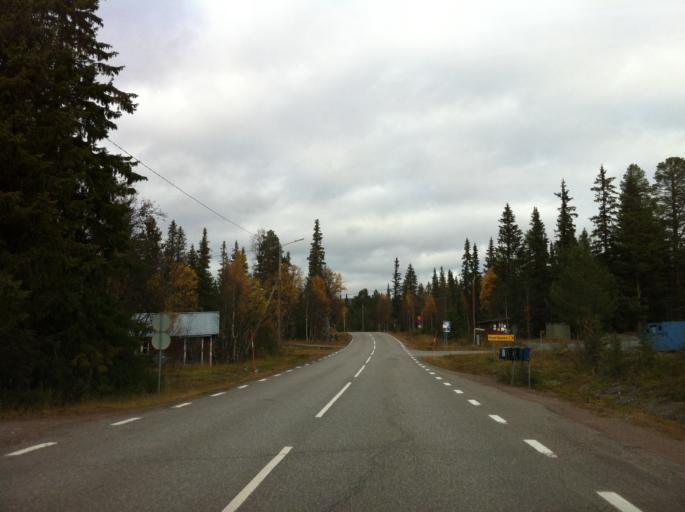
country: NO
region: Hedmark
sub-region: Engerdal
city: Engerdal
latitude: 62.0708
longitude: 12.3110
